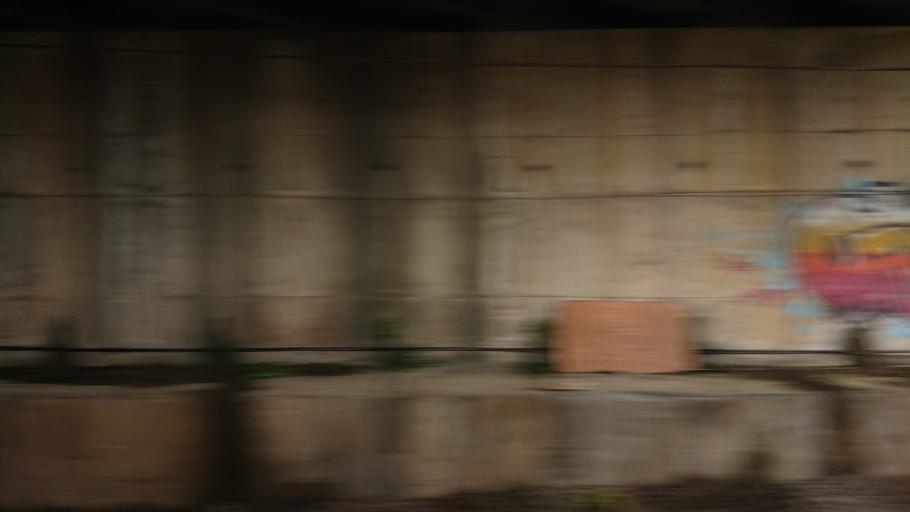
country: TW
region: Taiwan
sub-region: Keelung
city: Keelung
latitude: 25.0781
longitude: 121.6903
